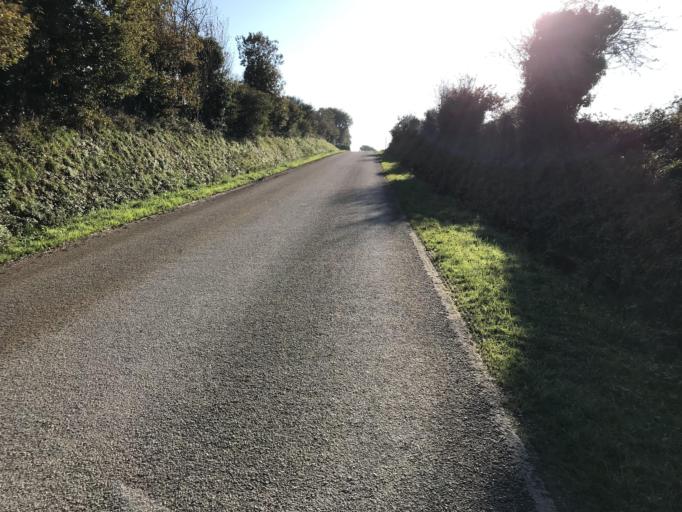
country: FR
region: Brittany
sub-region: Departement du Finistere
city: Hopital-Camfrout
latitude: 48.3086
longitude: -4.2307
